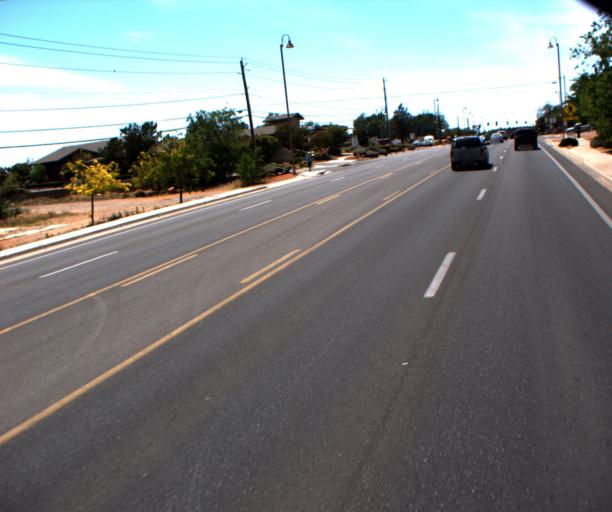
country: US
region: Arizona
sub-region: Yavapai County
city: West Sedona
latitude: 34.8632
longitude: -111.8021
